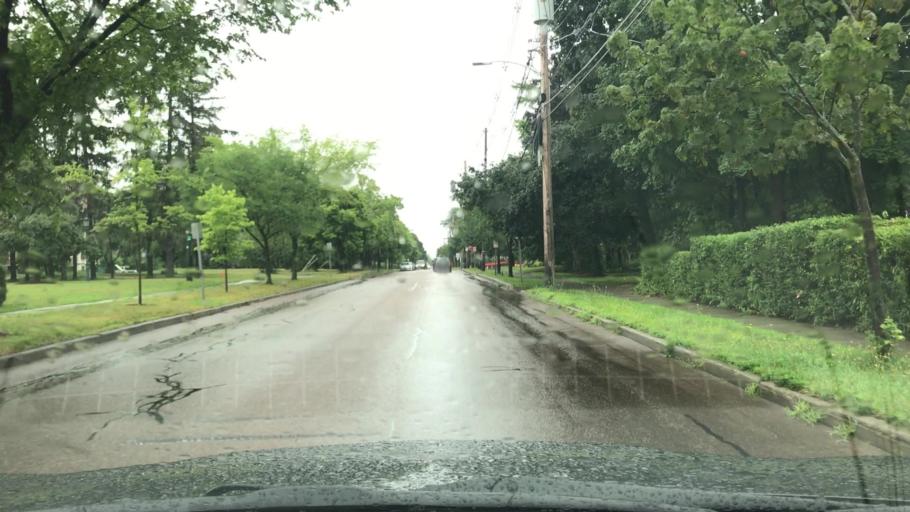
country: US
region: Vermont
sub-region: Chittenden County
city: Burlington
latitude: 44.4751
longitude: -73.2007
